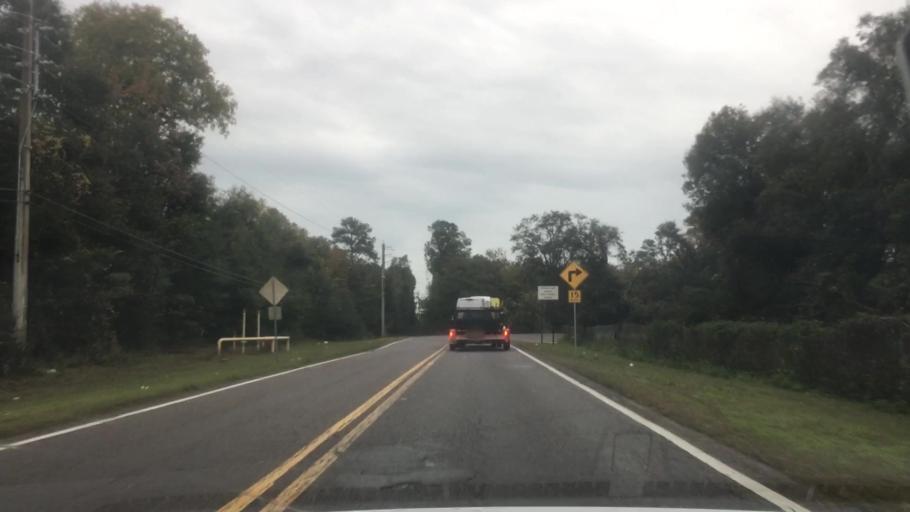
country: US
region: Florida
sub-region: Duval County
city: Jacksonville
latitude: 30.4130
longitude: -81.5619
